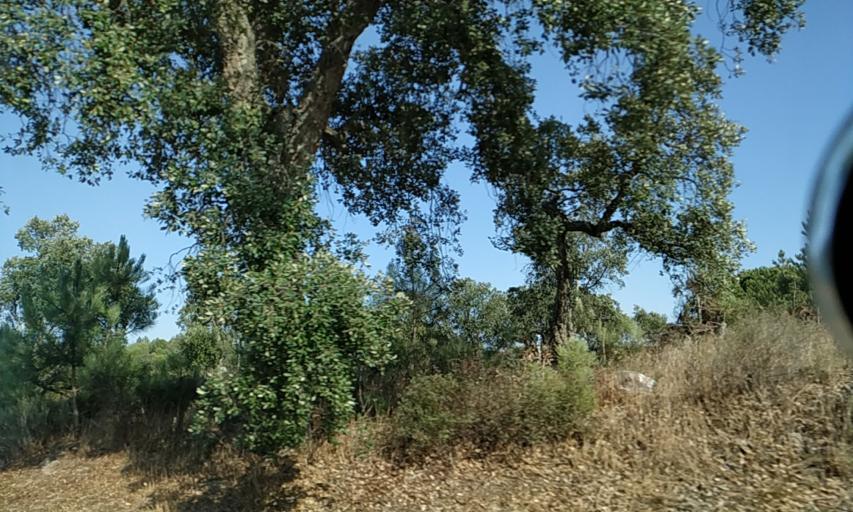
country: PT
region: Santarem
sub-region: Coruche
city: Coruche
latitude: 38.8845
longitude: -8.5376
